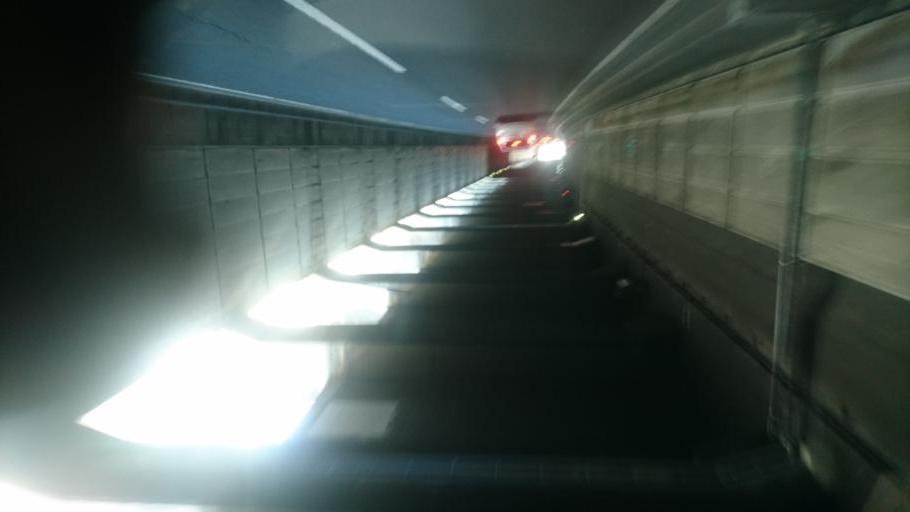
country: JP
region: Miyagi
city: Tomiya
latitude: 38.3329
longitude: 140.8862
